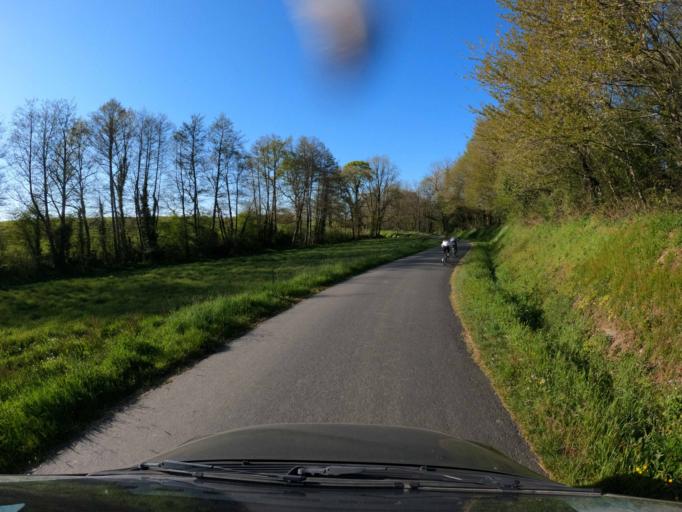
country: FR
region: Pays de la Loire
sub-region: Departement de la Vendee
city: Les Brouzils
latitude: 46.8863
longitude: -1.3389
